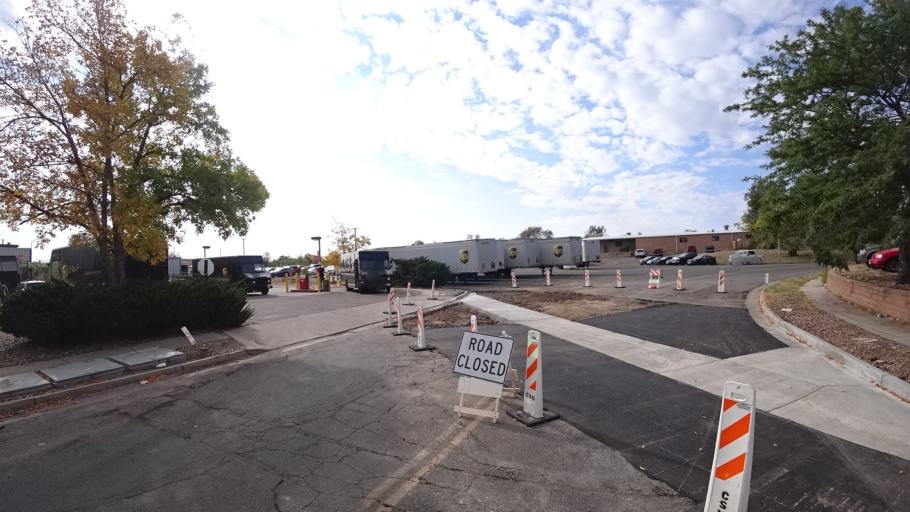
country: US
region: Colorado
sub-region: El Paso County
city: Cimarron Hills
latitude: 38.8451
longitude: -104.7458
